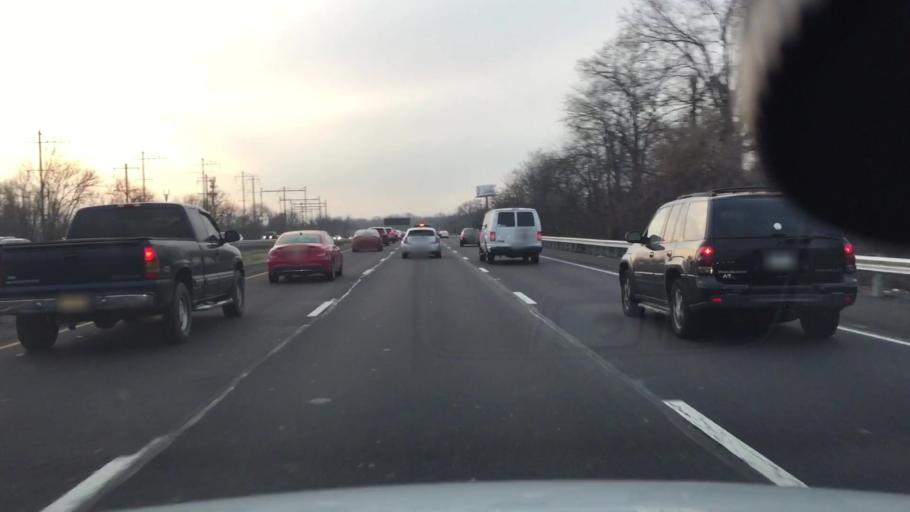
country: US
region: New Jersey
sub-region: Burlington County
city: Delanco
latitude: 40.0631
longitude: -74.9733
